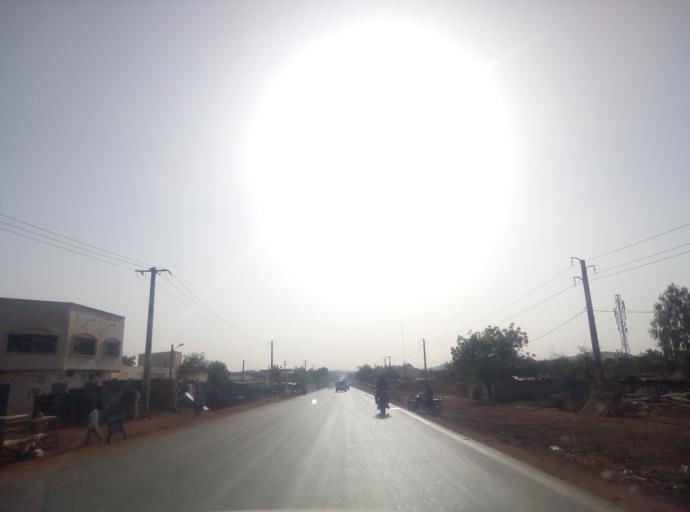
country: ML
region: Bamako
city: Bamako
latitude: 12.5872
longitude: -7.8331
